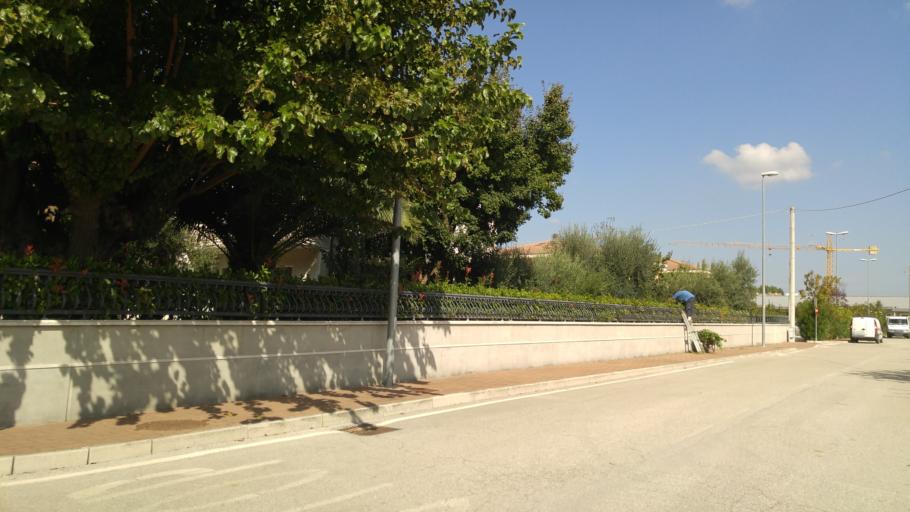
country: IT
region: The Marches
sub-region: Provincia di Pesaro e Urbino
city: Lucrezia
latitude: 43.7697
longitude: 12.9385
